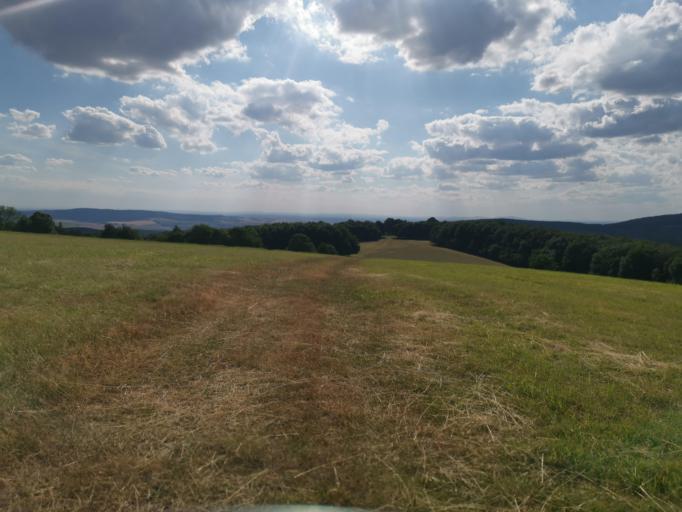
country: CZ
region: South Moravian
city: Knezdub
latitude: 48.7944
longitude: 17.3877
